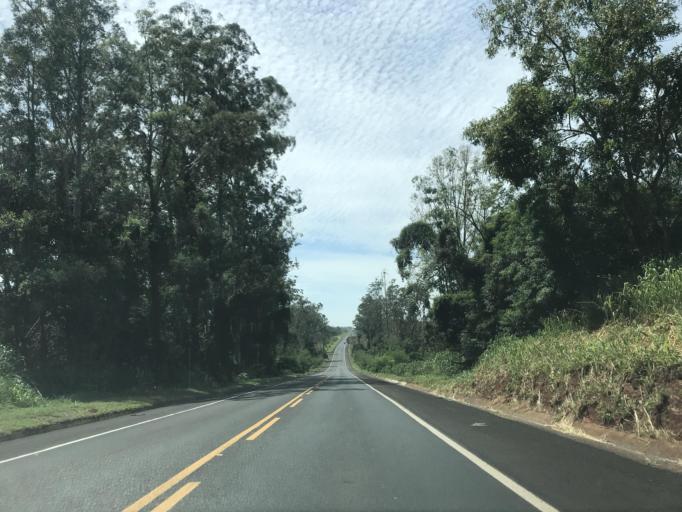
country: BR
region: Parana
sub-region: Paranavai
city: Paranavai
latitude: -22.9984
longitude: -52.5720
